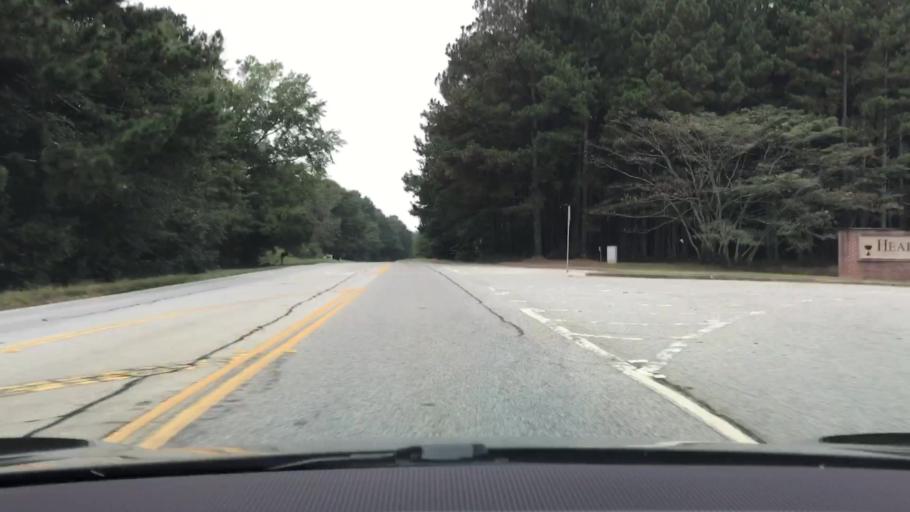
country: US
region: Georgia
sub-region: Barrow County
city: Russell
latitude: 33.9624
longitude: -83.6717
